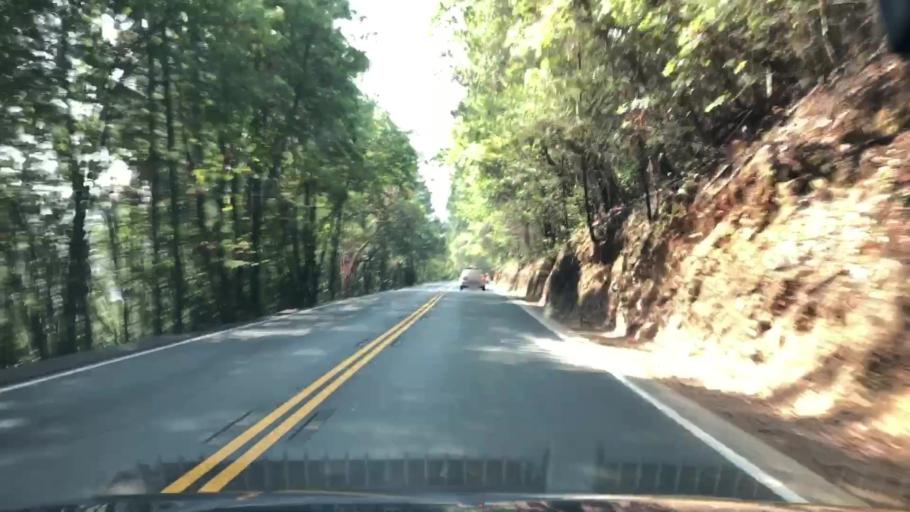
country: US
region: California
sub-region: Napa County
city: Calistoga
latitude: 38.6175
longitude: -122.5971
